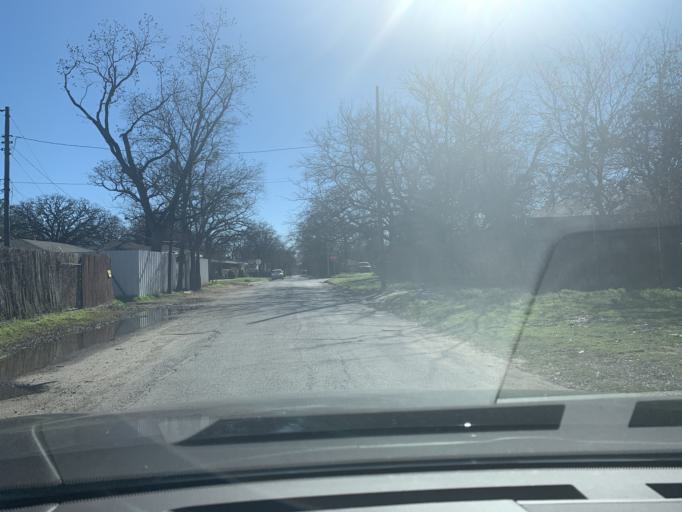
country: US
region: Texas
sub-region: Tarrant County
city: Haltom City
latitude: 32.7639
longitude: -97.2905
